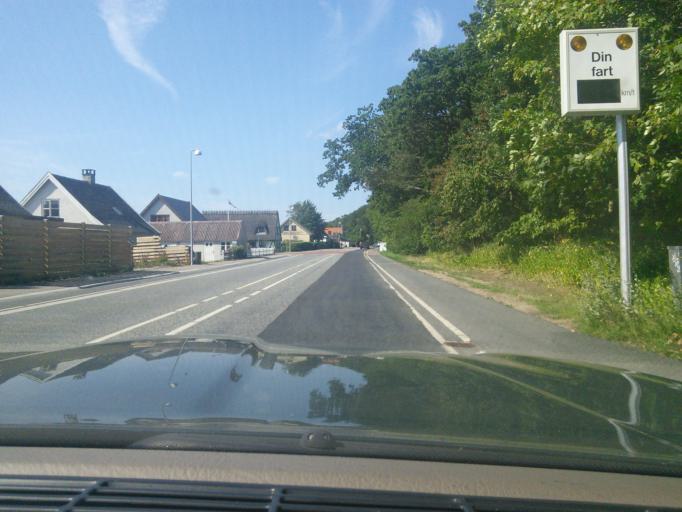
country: DK
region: Capital Region
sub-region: Halsnaes Kommune
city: Frederiksvaerk
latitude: 55.9845
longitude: 12.0192
